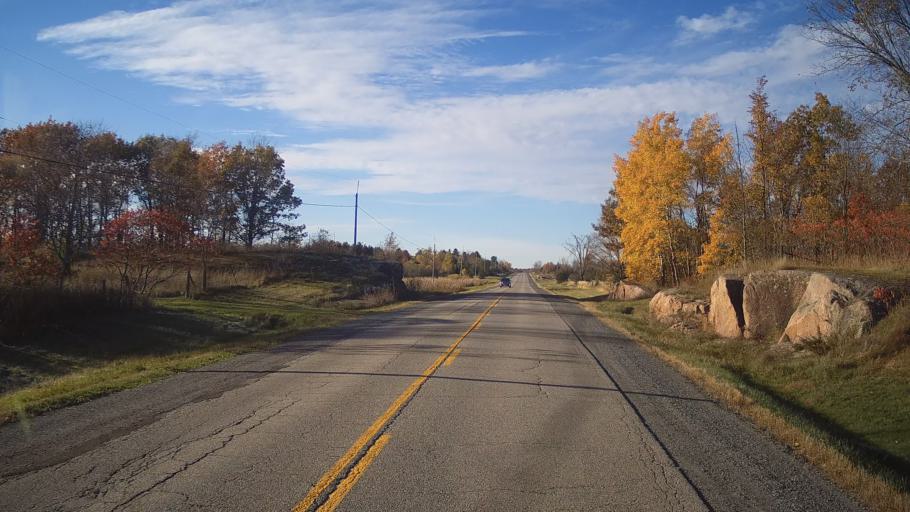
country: CA
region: Ontario
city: Perth
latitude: 44.7085
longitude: -76.4328
